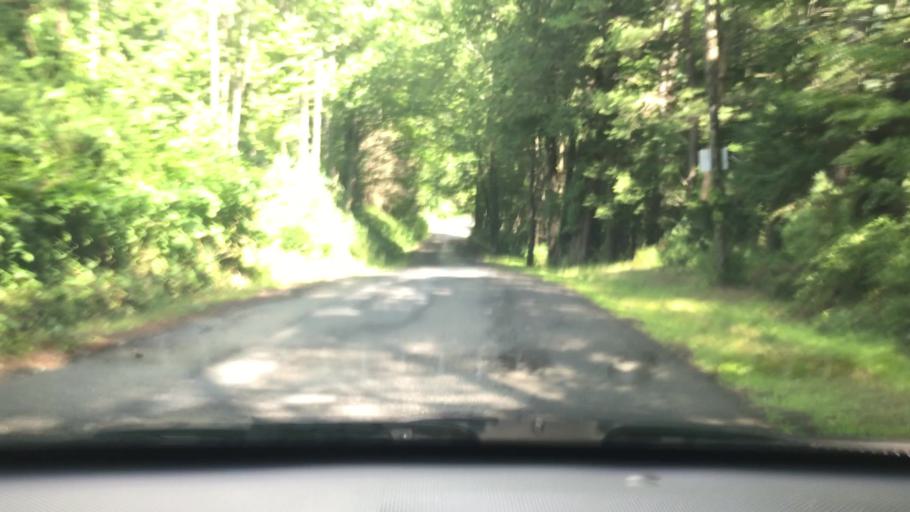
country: US
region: New York
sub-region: Ulster County
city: Shokan
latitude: 41.9652
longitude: -74.2852
